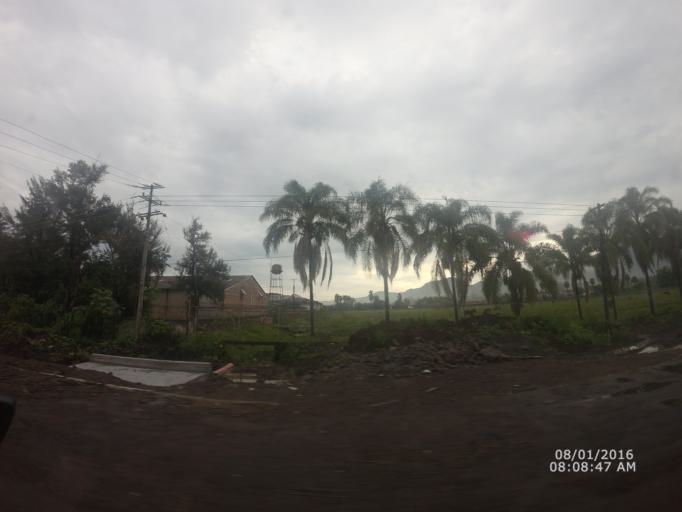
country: MX
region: Nayarit
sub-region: Tepic
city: La Corregidora
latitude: 21.4560
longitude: -104.8227
